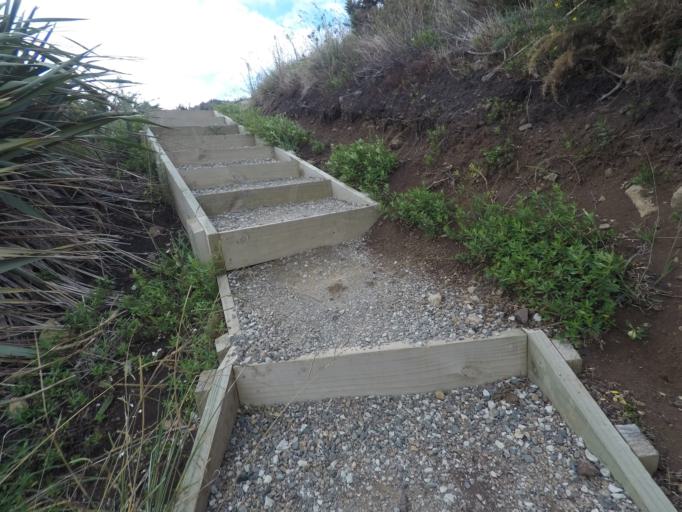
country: NZ
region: Auckland
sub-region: Auckland
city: Titirangi
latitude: -37.0409
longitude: 174.5121
